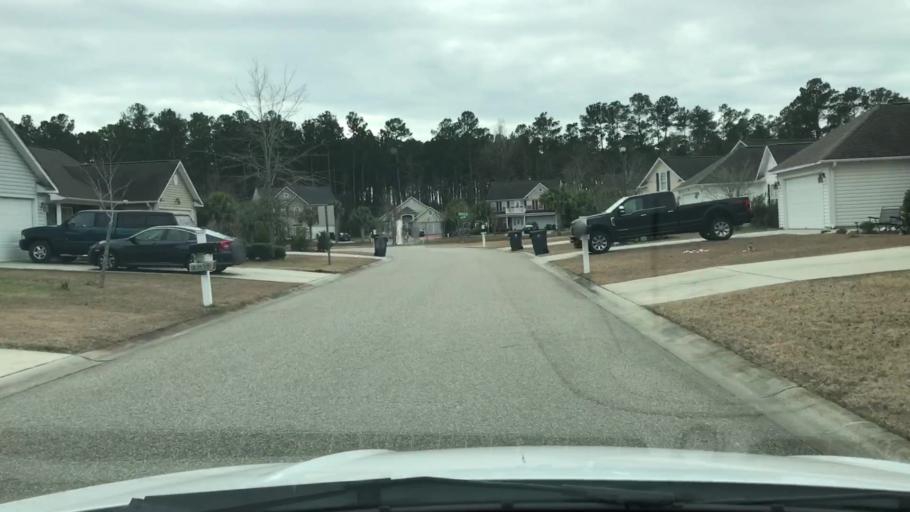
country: US
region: South Carolina
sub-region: Horry County
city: Socastee
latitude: 33.6704
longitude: -78.9740
